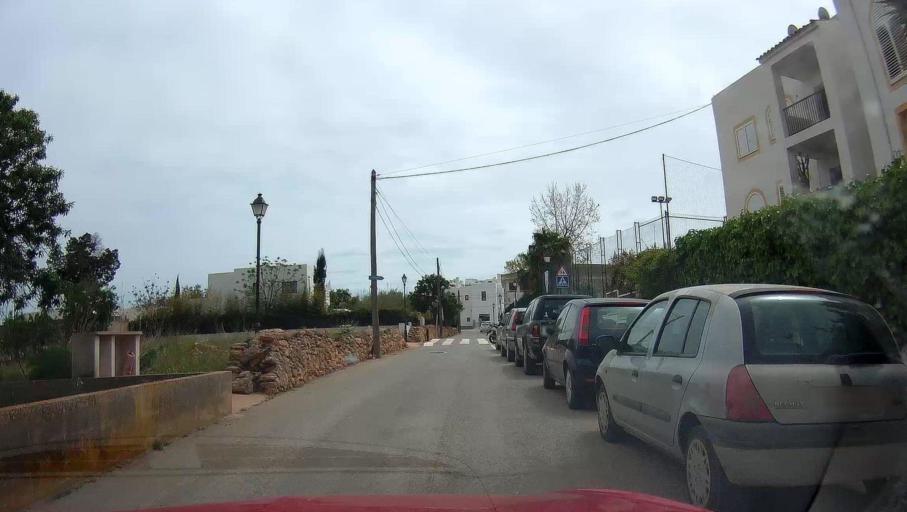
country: ES
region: Balearic Islands
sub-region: Illes Balears
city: Ibiza
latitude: 39.0004
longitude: 1.4293
